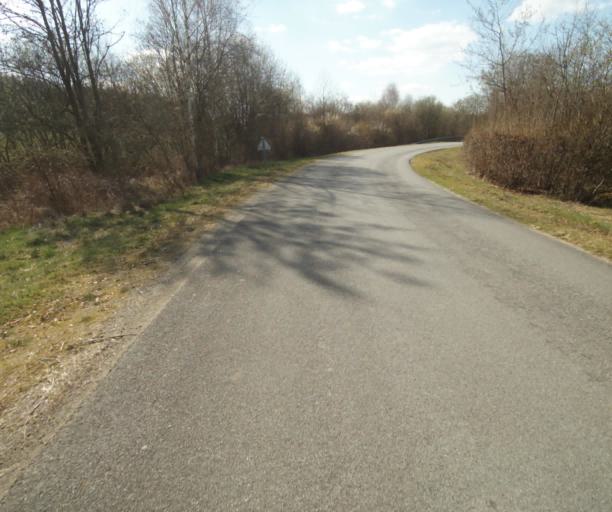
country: FR
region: Limousin
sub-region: Departement de la Correze
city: Saint-Mexant
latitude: 45.3032
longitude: 1.6574
